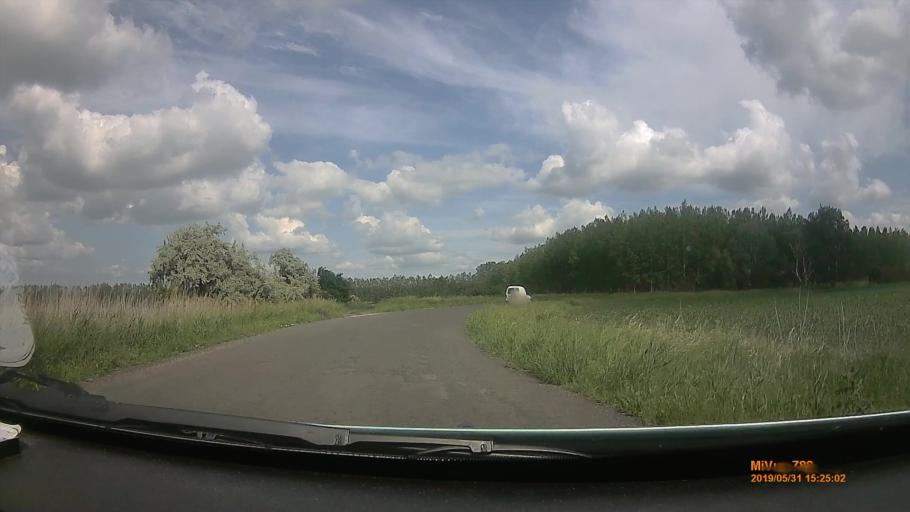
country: HU
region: Borsod-Abauj-Zemplen
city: Taktaharkany
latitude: 48.0664
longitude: 21.1627
